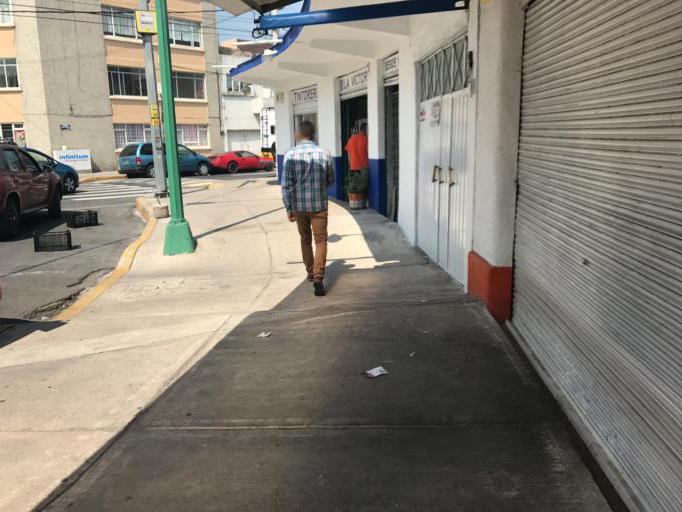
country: MX
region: Mexico
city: Colonia Lindavista
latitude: 19.4745
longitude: -99.1245
